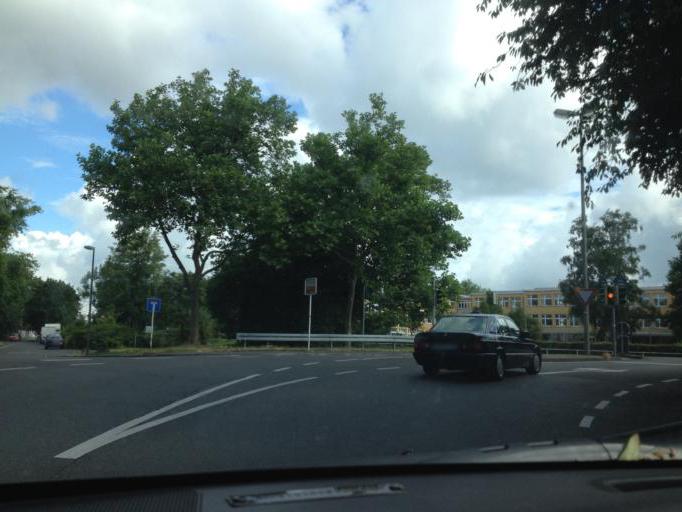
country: DE
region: North Rhine-Westphalia
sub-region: Regierungsbezirk Arnsberg
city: Dortmund
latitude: 51.4728
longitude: 7.4506
